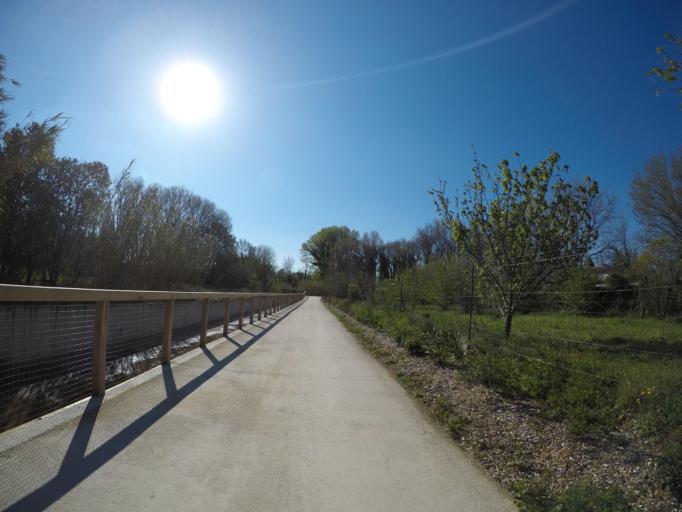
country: FR
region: Languedoc-Roussillon
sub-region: Departement des Pyrenees-Orientales
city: Saint-Esteve
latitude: 42.7001
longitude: 2.8568
